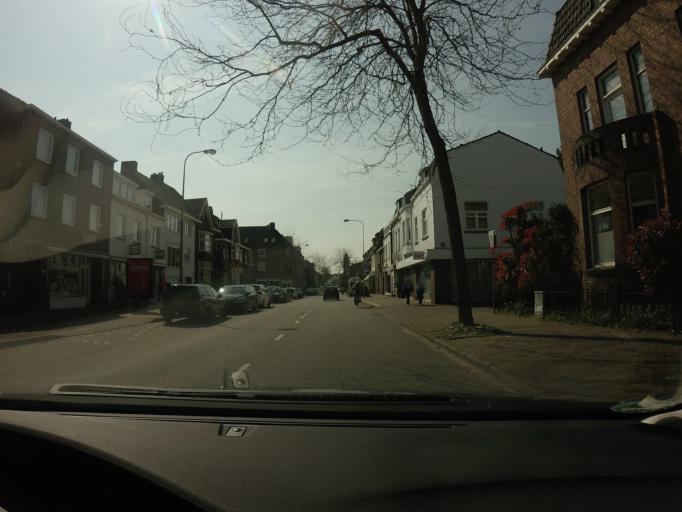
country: NL
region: Limburg
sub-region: Gemeente Maastricht
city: Heer
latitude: 50.8453
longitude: 5.7276
